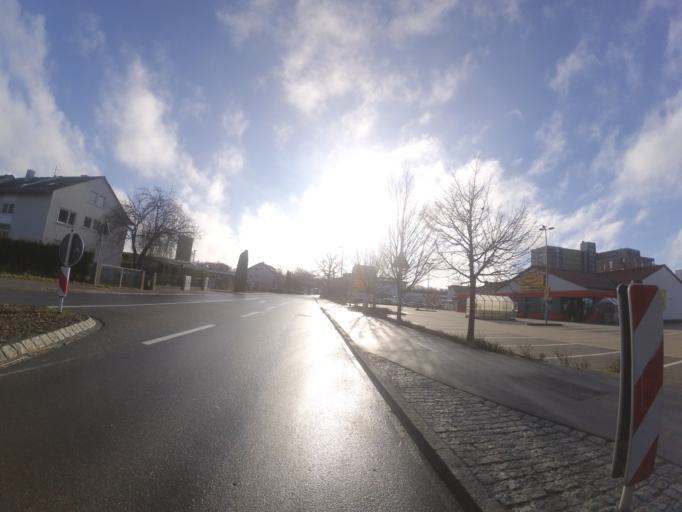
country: DE
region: Bavaria
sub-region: Swabia
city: Neu-Ulm
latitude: 48.4367
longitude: 10.0570
